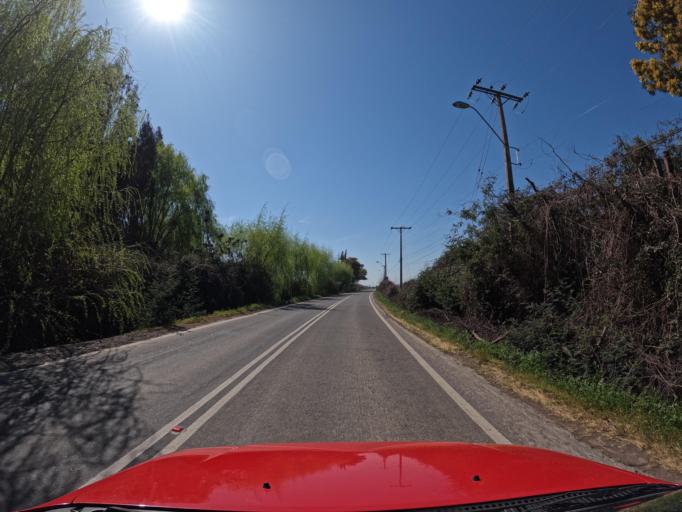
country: CL
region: Maule
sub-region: Provincia de Curico
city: Rauco
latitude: -35.0333
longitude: -71.4447
